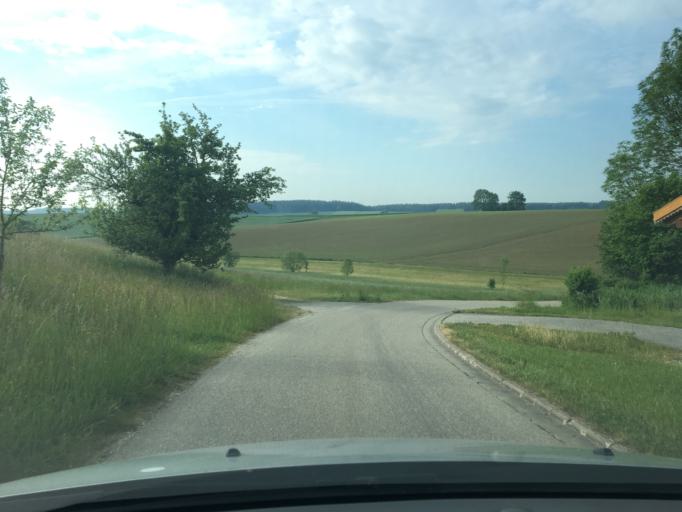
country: DE
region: Bavaria
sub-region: Upper Bavaria
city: Egglkofen
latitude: 48.4051
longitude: 12.4324
